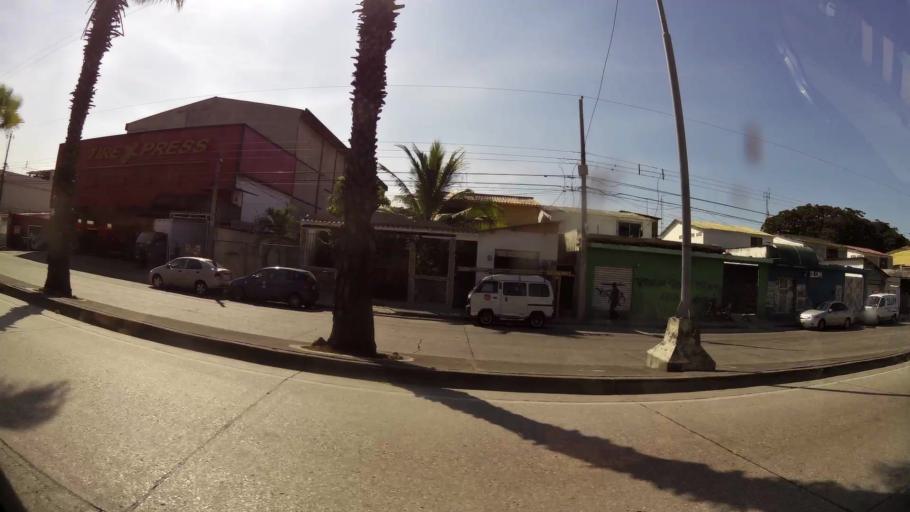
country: EC
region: Guayas
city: Eloy Alfaro
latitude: -2.1344
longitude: -79.9076
